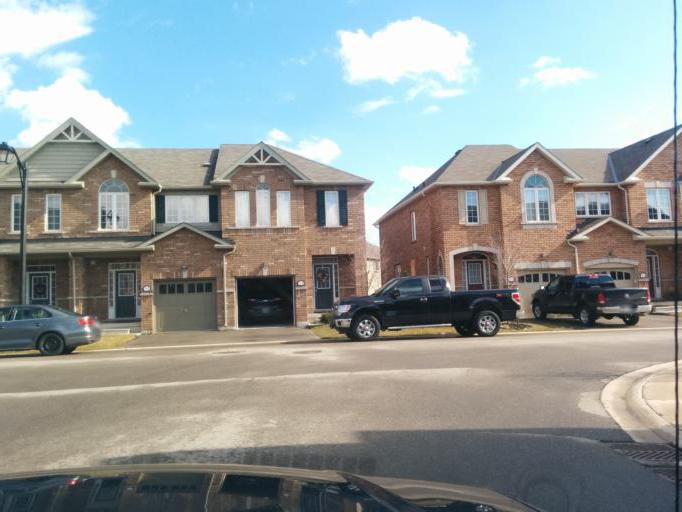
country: CA
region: Ontario
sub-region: Halton
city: Milton
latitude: 43.4988
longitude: -79.8661
